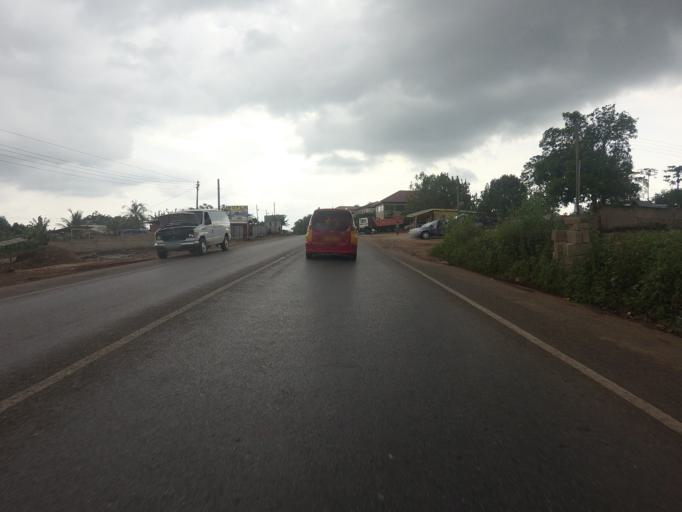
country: GH
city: Akropong
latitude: 5.9290
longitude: -0.1284
